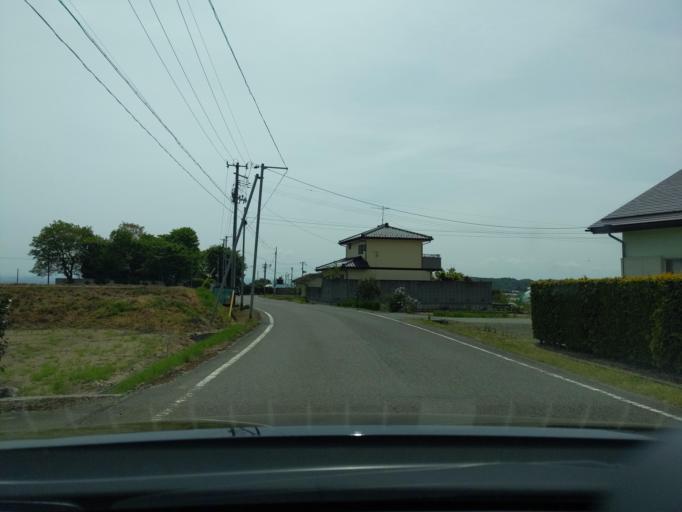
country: JP
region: Fukushima
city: Koriyama
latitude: 37.4036
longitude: 140.2609
